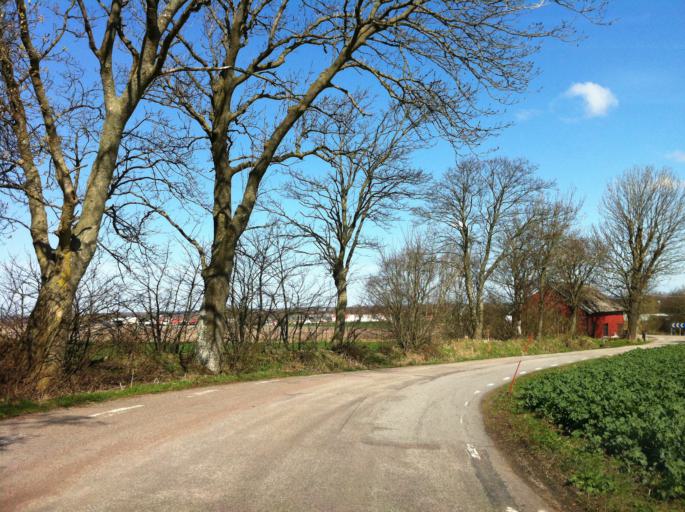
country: SE
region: Skane
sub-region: Helsingborg
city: Glumslov
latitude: 55.9432
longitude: 12.8404
